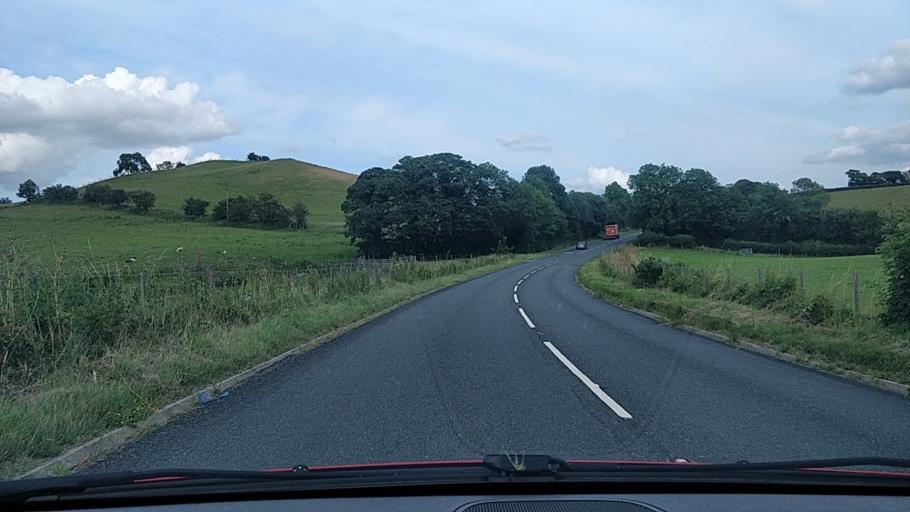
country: GB
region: Wales
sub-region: Denbighshire
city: Corwen
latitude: 52.9975
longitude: -3.3668
